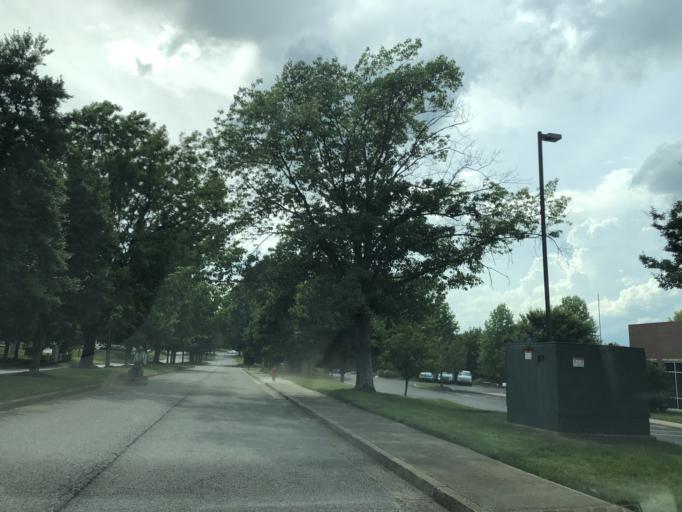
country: US
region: Tennessee
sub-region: Davidson County
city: Oak Hill
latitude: 36.0865
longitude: -86.7496
